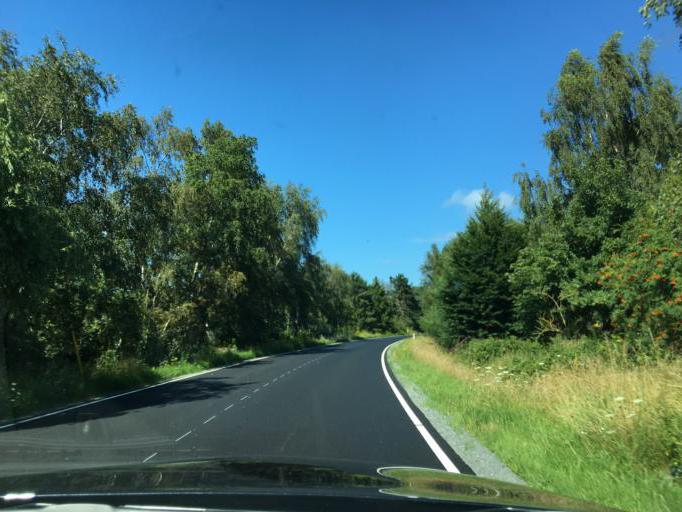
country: DK
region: Capital Region
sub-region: Gribskov Kommune
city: Helsinge
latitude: 56.0889
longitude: 12.1721
